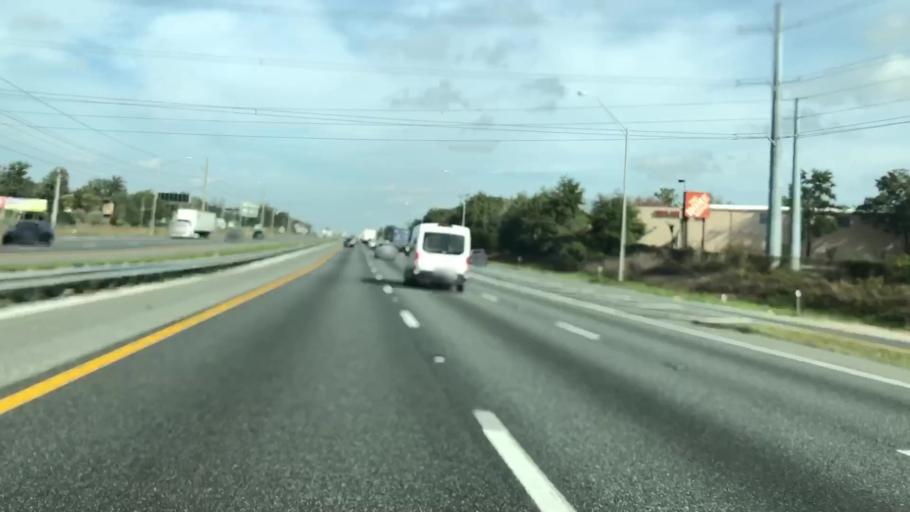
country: US
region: Florida
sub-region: Marion County
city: Ocala
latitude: 29.1537
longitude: -82.1847
